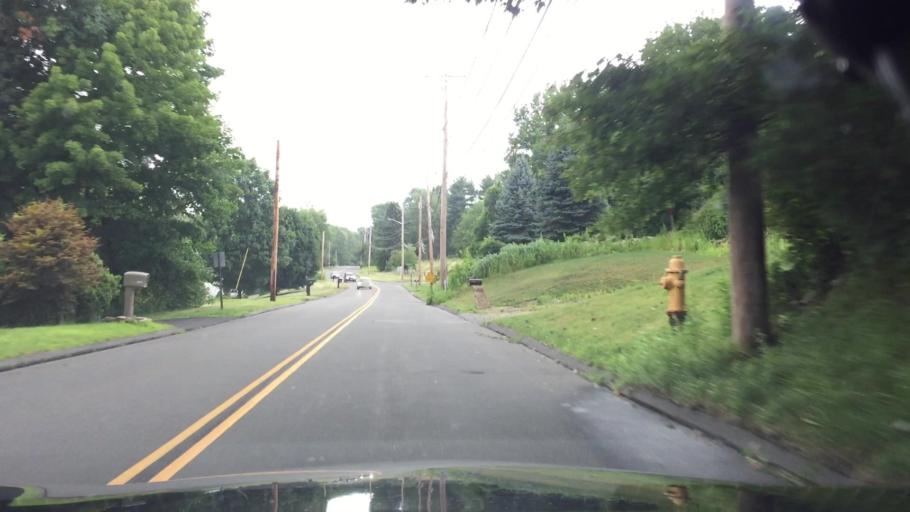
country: US
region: Connecticut
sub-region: New Haven County
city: City of Milford (balance)
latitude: 41.2552
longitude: -73.1188
